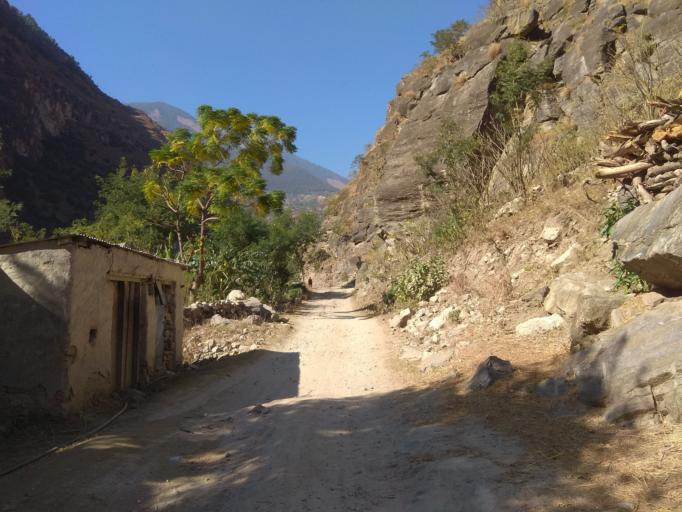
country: NP
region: Far Western
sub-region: Seti Zone
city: Achham
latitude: 29.2190
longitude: 81.6337
